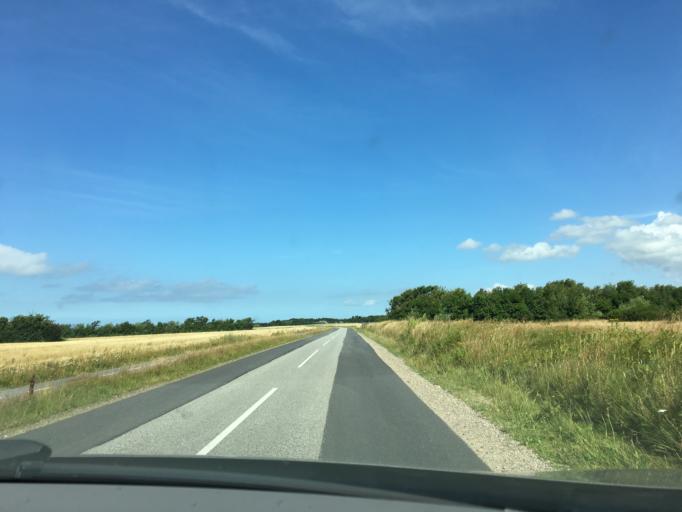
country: DK
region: Central Jutland
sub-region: Ringkobing-Skjern Kommune
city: Skjern
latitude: 55.9749
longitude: 8.3559
